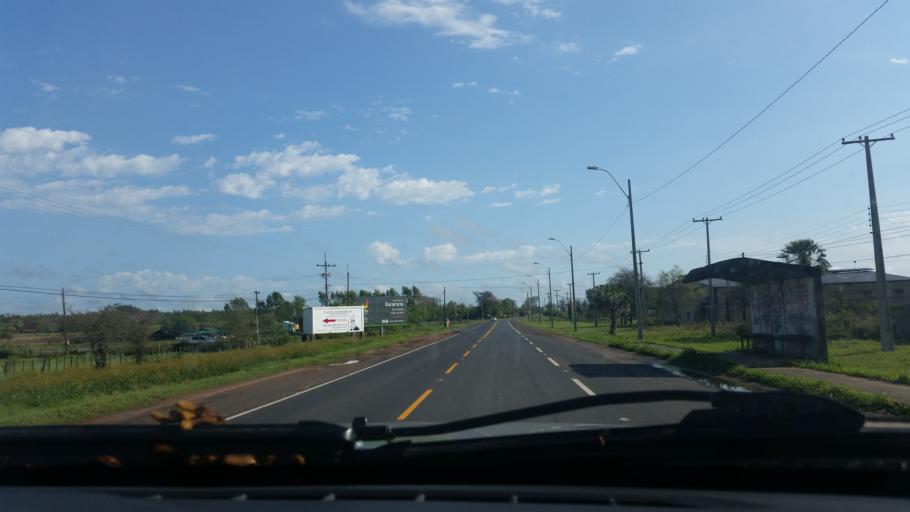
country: PY
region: Presidente Hayes
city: Villa Hayes
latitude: -25.0664
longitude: -57.5335
